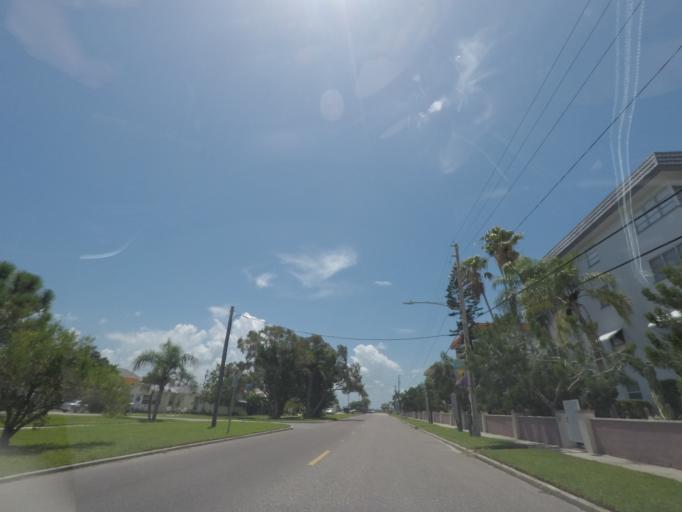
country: US
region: Florida
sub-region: Pinellas County
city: Gulfport
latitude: 27.7392
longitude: -82.7120
